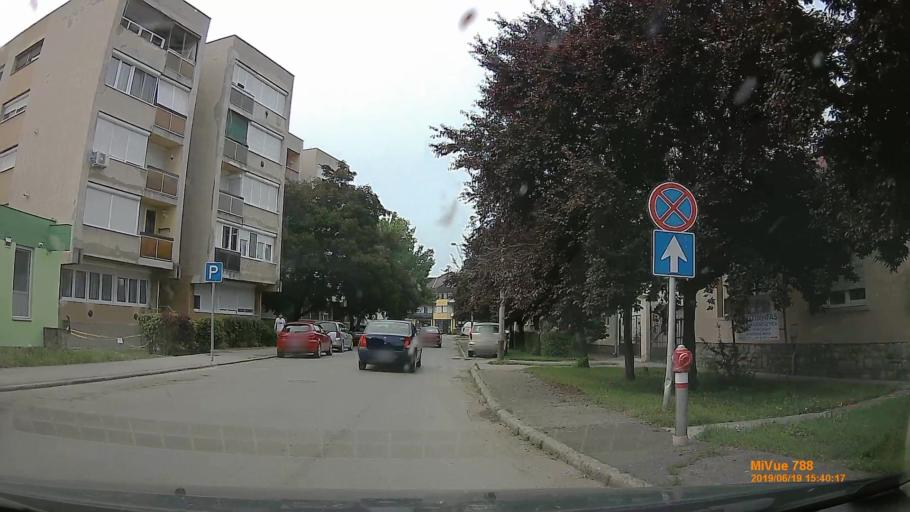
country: HU
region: Baranya
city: Szigetvar
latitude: 46.0466
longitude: 17.8060
